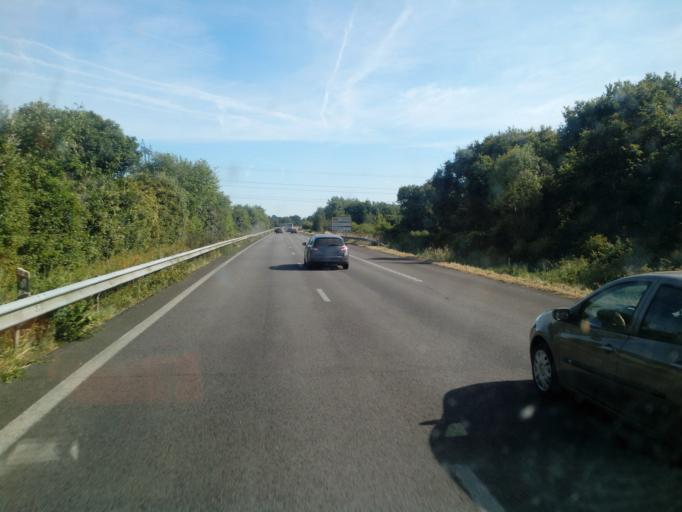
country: FR
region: Pays de la Loire
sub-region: Departement de la Loire-Atlantique
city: Heric
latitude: 47.4282
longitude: -1.6376
